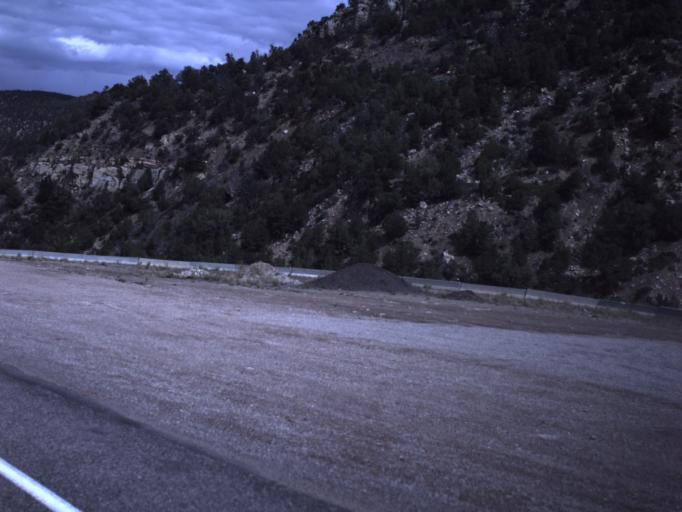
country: US
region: Utah
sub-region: Iron County
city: Cedar City
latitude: 37.6344
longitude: -112.9443
